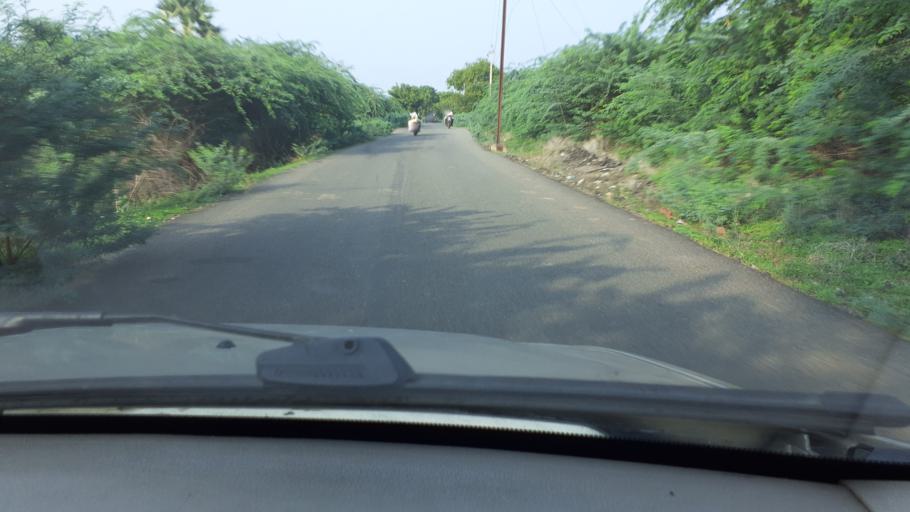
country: IN
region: Tamil Nadu
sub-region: Thoothukkudi
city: Alwar Tirunagari
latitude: 8.5795
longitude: 77.9773
